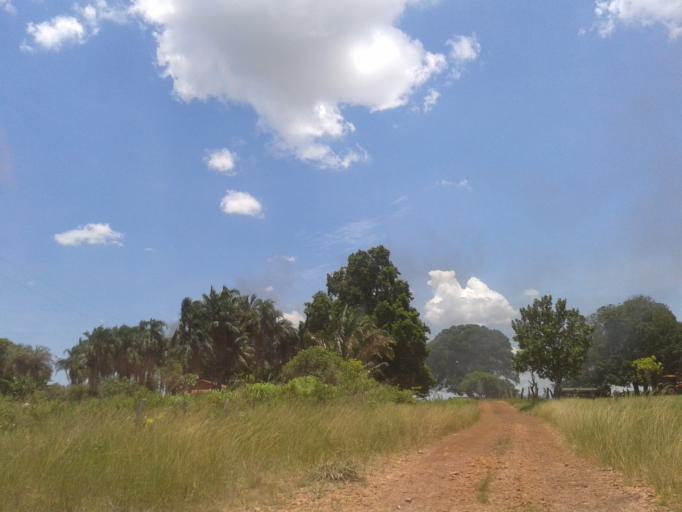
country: BR
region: Minas Gerais
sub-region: Santa Vitoria
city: Santa Vitoria
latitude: -19.2260
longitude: -50.4552
